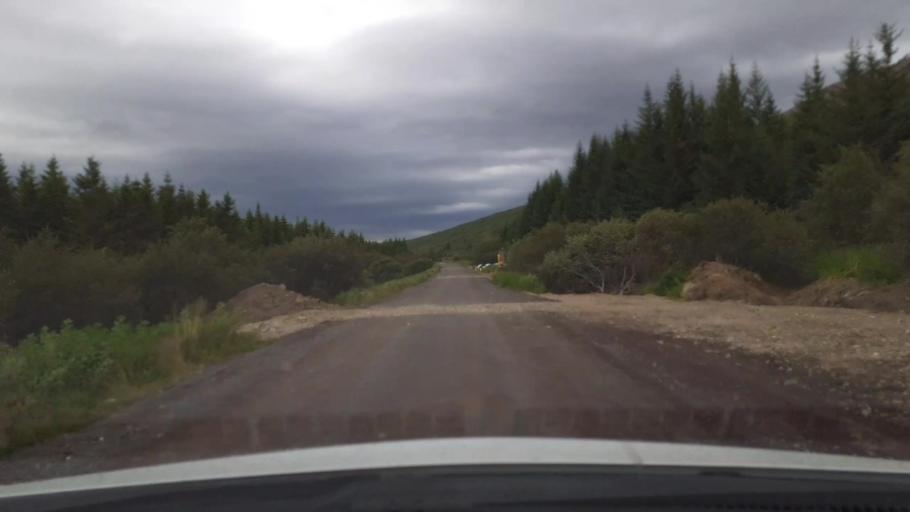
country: IS
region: West
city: Borgarnes
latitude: 64.5386
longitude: -21.5326
